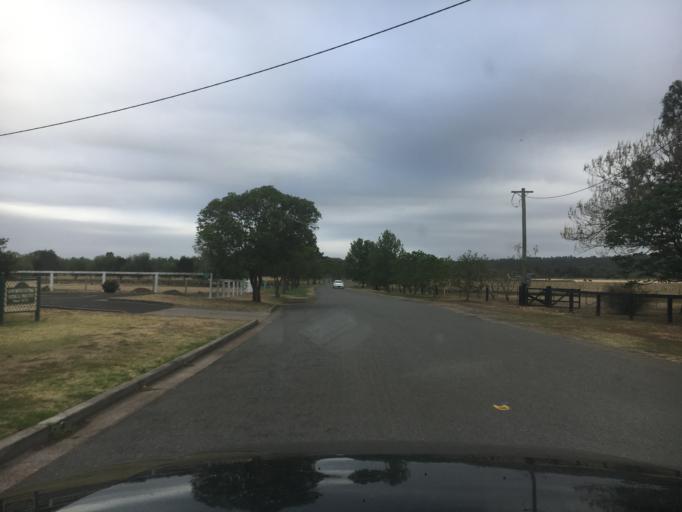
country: AU
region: New South Wales
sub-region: Singleton
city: Singleton
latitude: -32.5658
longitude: 151.1888
